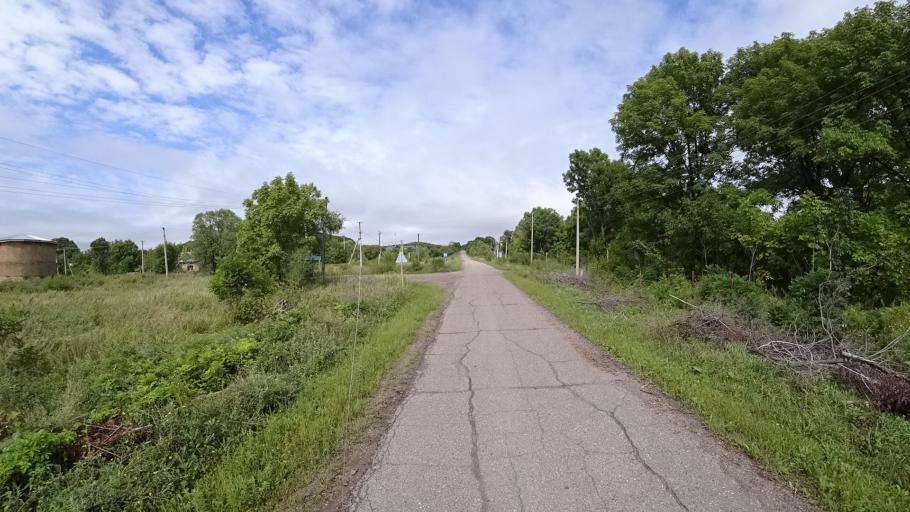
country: RU
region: Primorskiy
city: Lyalichi
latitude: 44.1375
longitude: 132.3877
